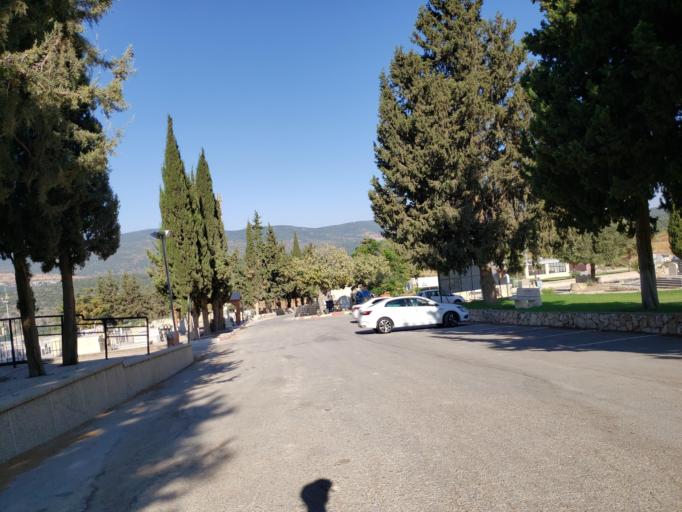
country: IL
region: Northern District
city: Safed
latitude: 32.9679
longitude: 35.4866
